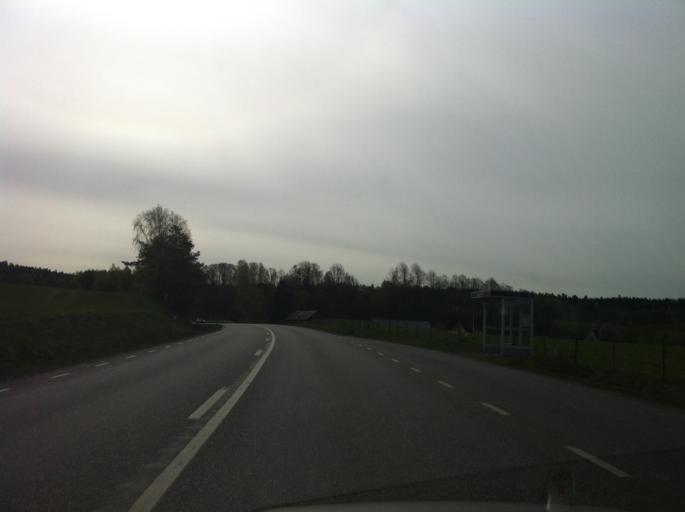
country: SE
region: Vaestra Goetaland
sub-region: Marks Kommun
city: Bua
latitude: 57.5218
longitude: 12.5449
